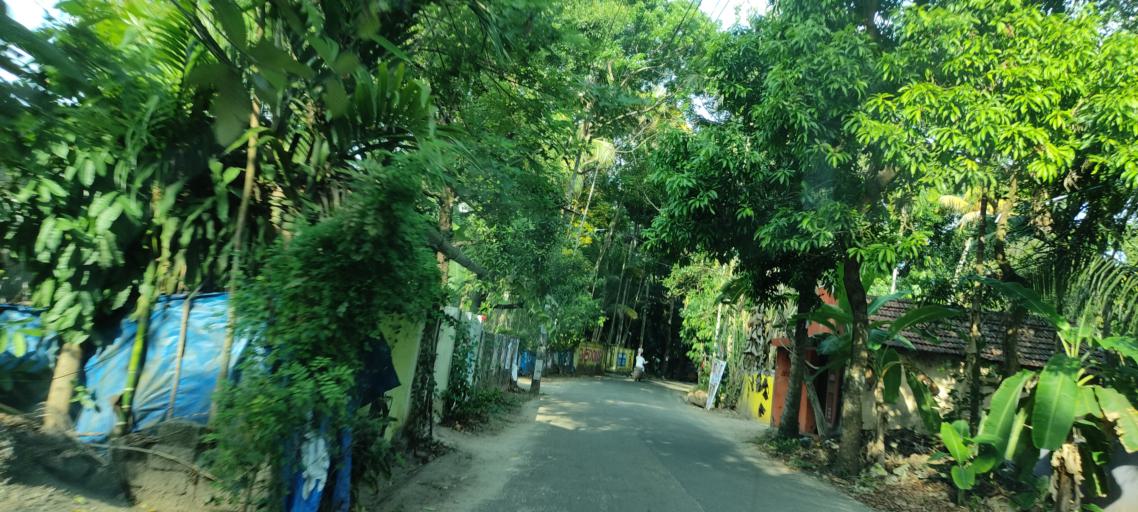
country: IN
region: Kerala
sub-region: Alappuzha
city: Vayalar
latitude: 9.7282
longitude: 76.2943
